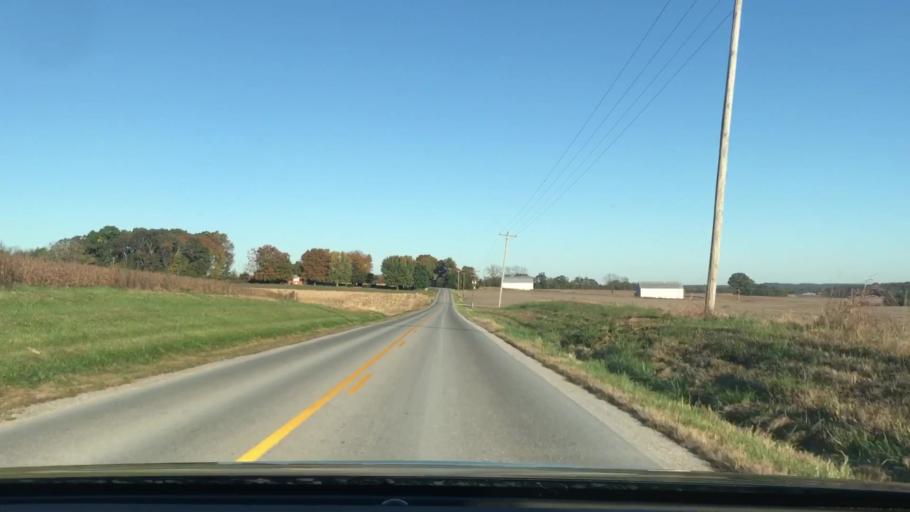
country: US
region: Kentucky
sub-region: Logan County
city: Auburn
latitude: 36.8416
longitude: -86.6941
